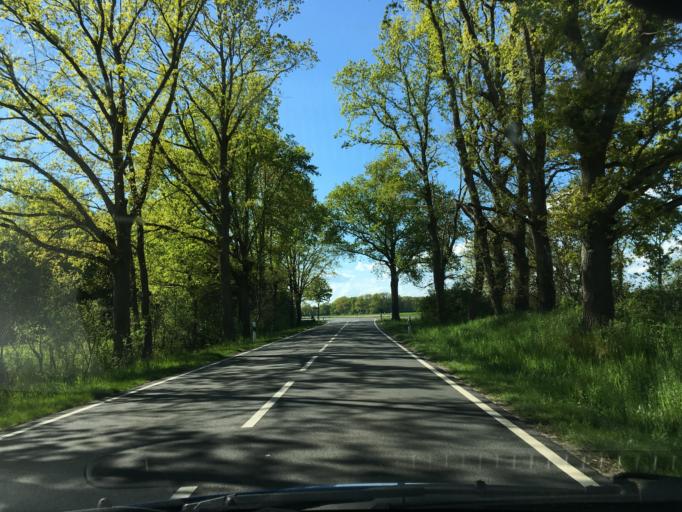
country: DE
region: Lower Saxony
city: Gartow
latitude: 53.0247
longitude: 11.4869
